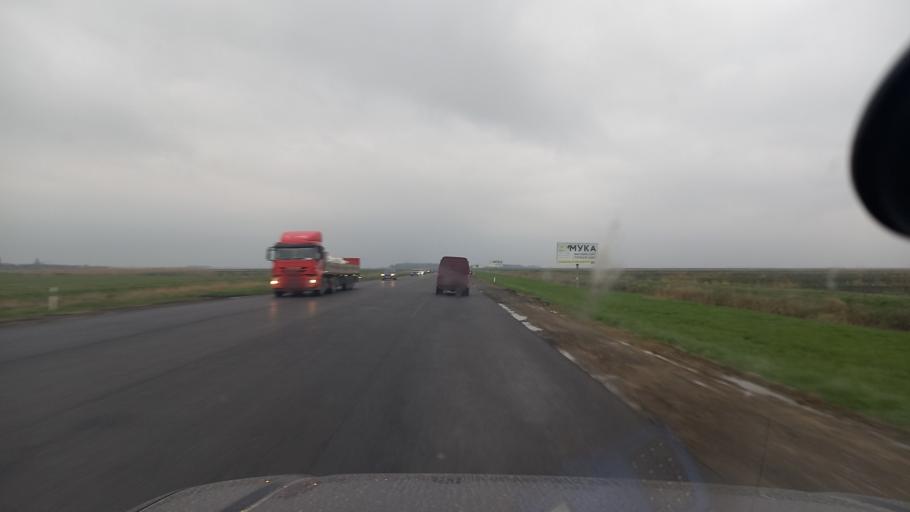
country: RU
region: Krasnodarskiy
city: Novomyshastovskaya
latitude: 45.1791
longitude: 38.5735
